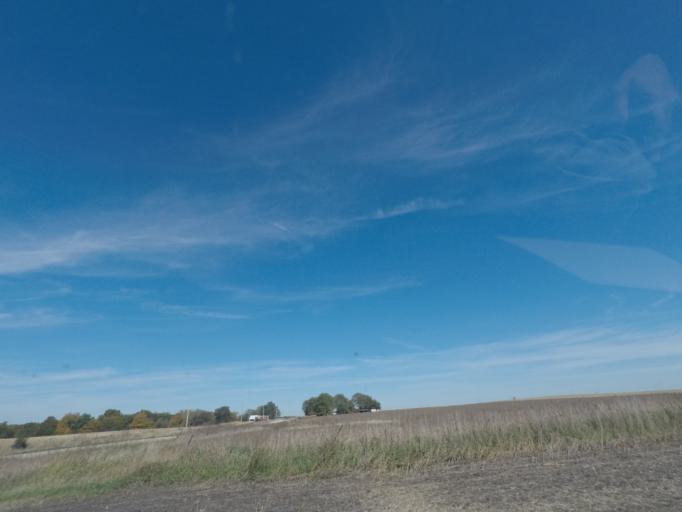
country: US
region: Iowa
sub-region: Story County
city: Nevada
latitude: 42.0414
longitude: -93.3594
